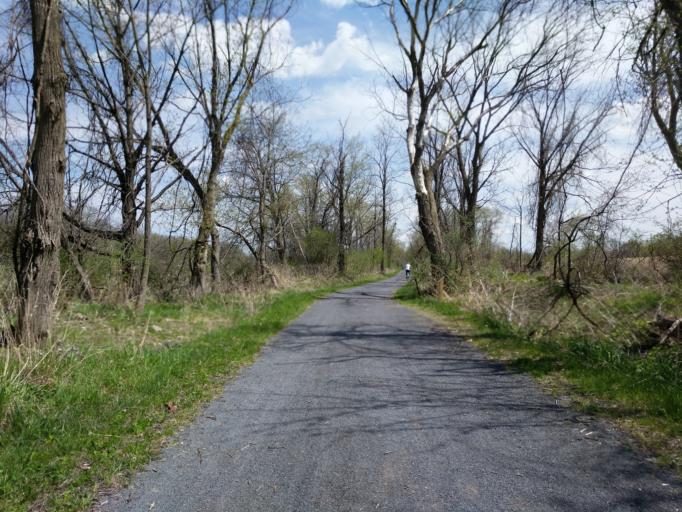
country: US
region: New York
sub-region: Tompkins County
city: Northwest Ithaca
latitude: 42.5173
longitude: -76.5712
